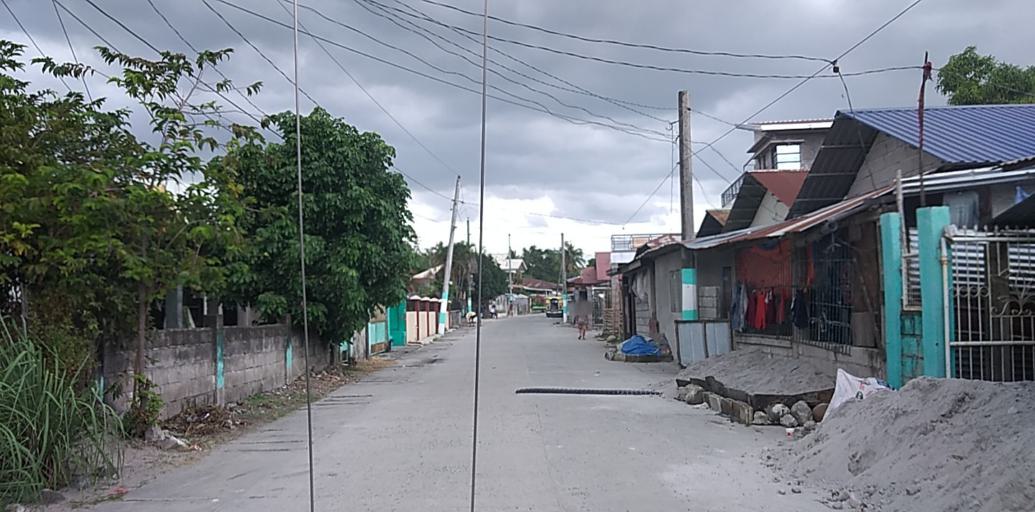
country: PH
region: Central Luzon
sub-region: Province of Pampanga
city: Pio
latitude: 15.0468
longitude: 120.5380
